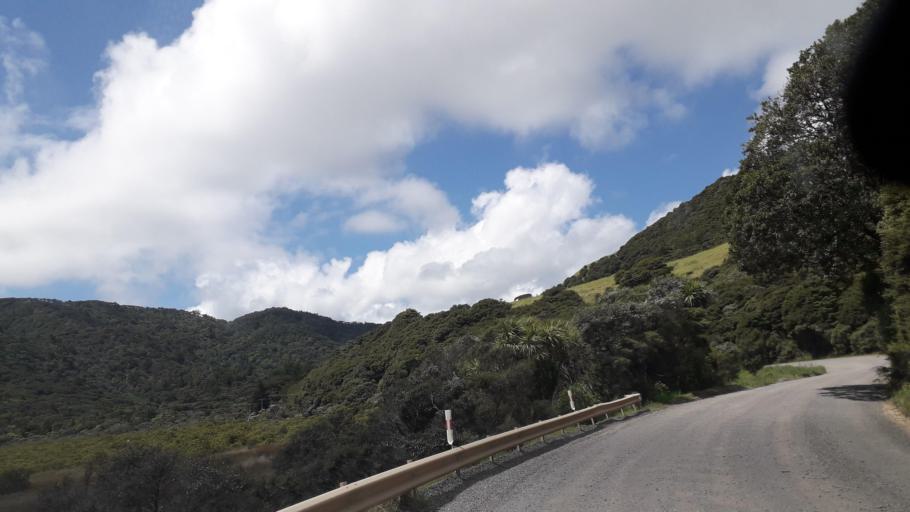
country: NZ
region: Northland
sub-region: Far North District
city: Paihia
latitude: -35.2598
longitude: 174.2647
